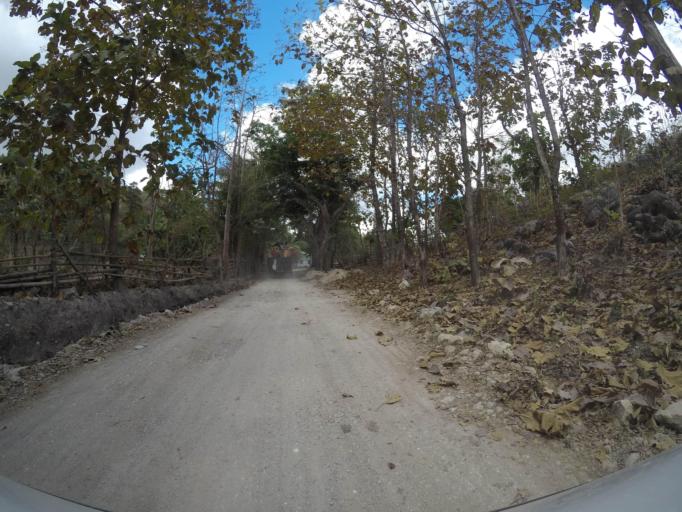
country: TL
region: Baucau
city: Baucau
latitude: -8.5122
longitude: 126.6854
